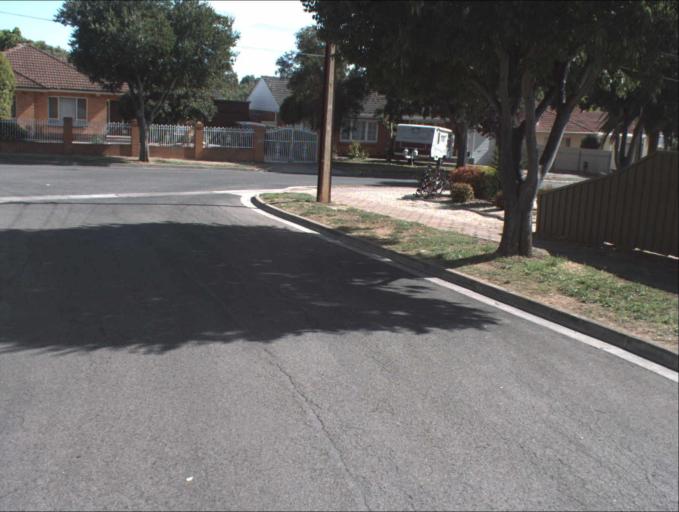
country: AU
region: South Australia
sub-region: Port Adelaide Enfield
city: Gilles Plains
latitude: -34.8662
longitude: 138.6534
